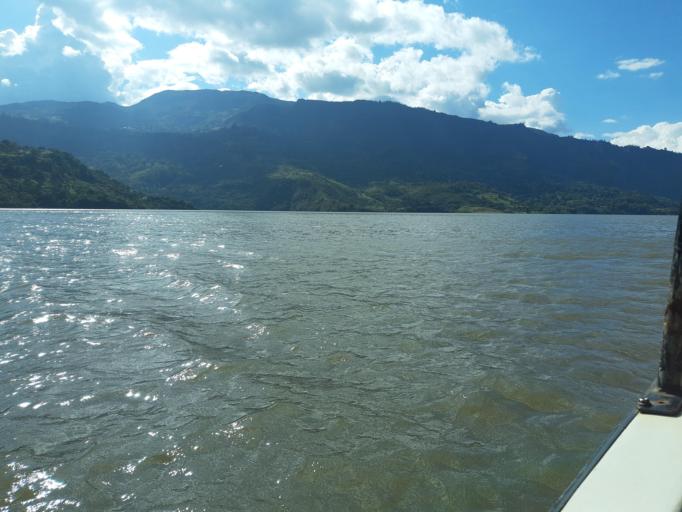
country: CO
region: Boyaca
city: Chivor
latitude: 4.9458
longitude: -73.3183
